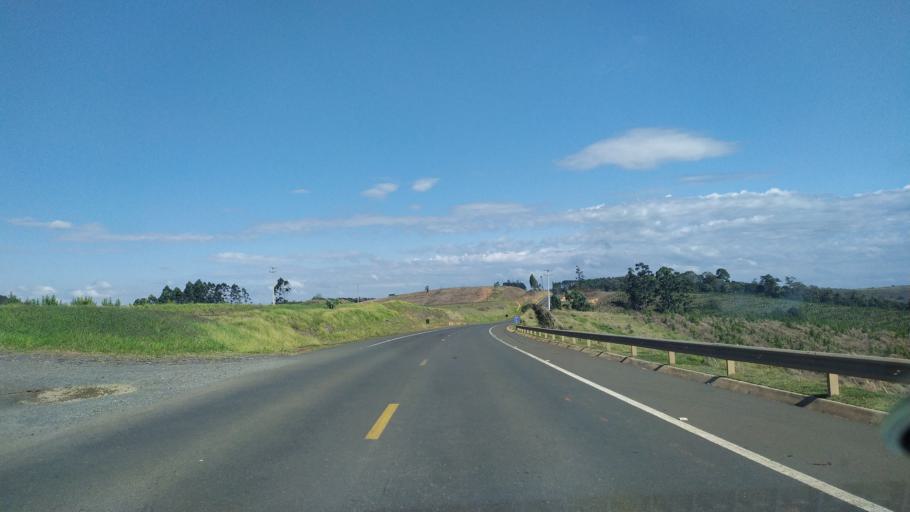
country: BR
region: Parana
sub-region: Ortigueira
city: Ortigueira
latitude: -24.2809
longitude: -50.8087
